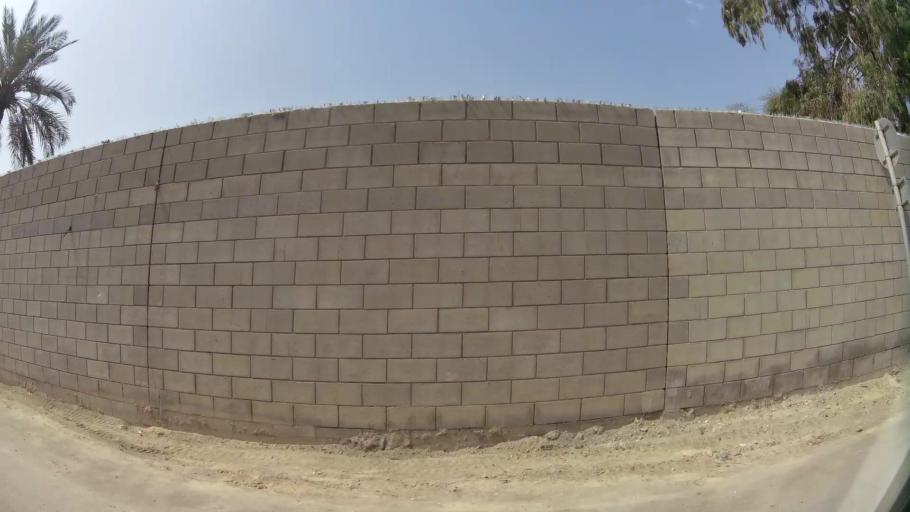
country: BH
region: Manama
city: Jidd Hafs
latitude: 26.2258
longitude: 50.4949
